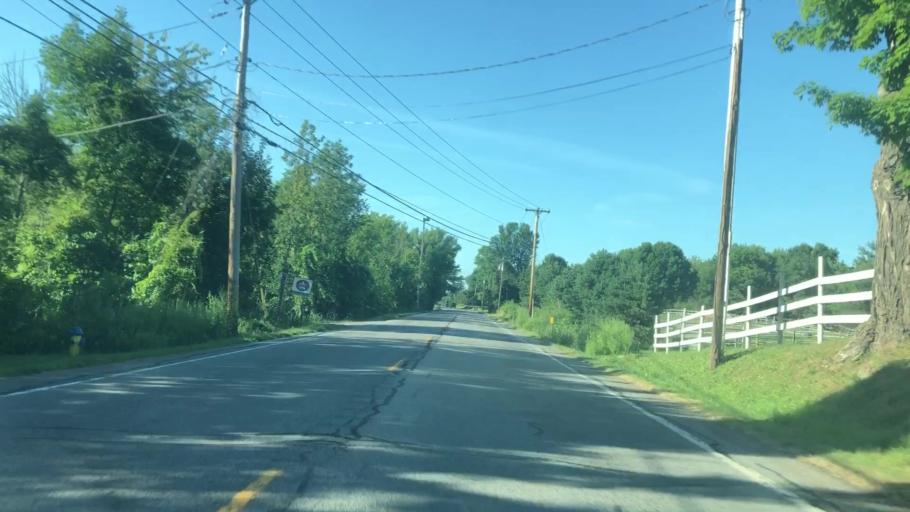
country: US
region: New York
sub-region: Wayne County
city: Ontario
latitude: 43.1569
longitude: -77.2915
